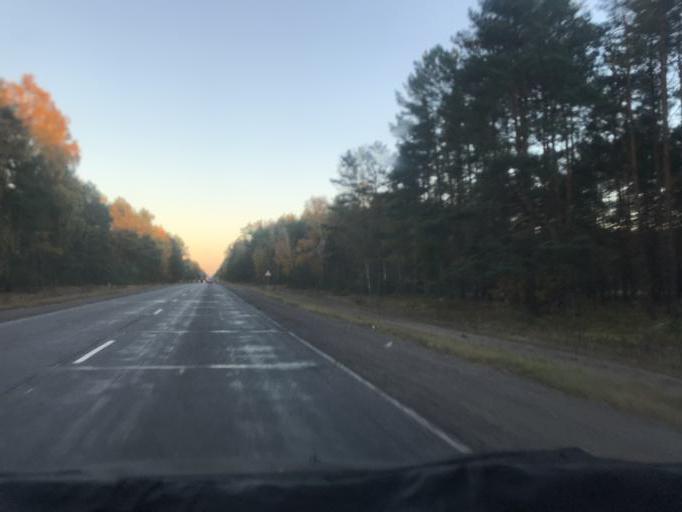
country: BY
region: Gomel
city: Mazyr
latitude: 52.2061
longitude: 29.0645
